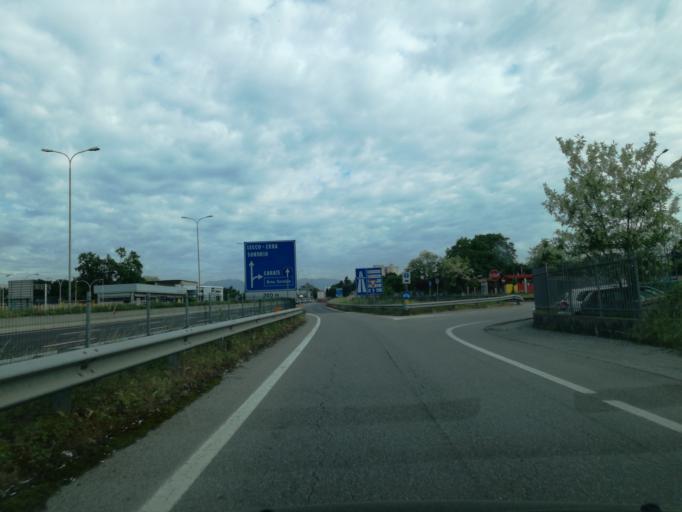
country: IT
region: Lombardy
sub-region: Provincia di Monza e Brianza
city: Santa Margherita
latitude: 45.6522
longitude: 9.2261
